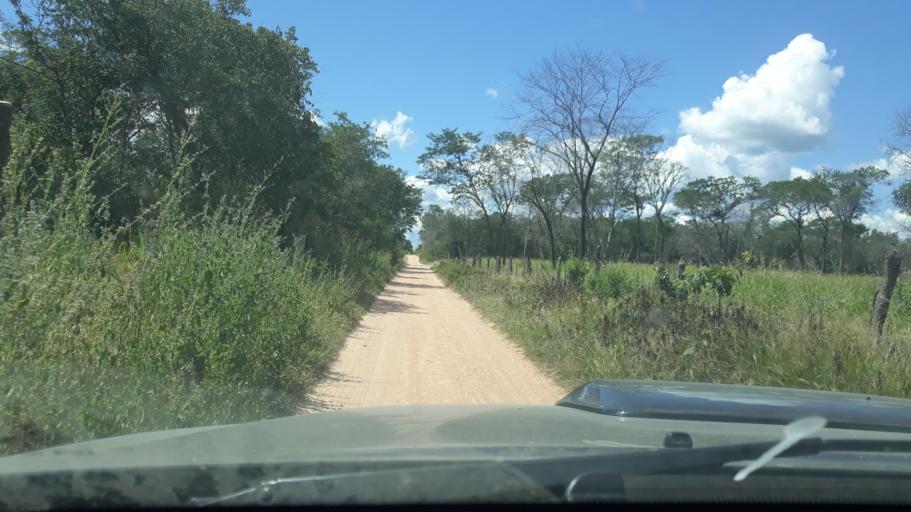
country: BR
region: Bahia
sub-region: Riacho De Santana
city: Riacho de Santana
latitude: -13.8666
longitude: -43.0181
